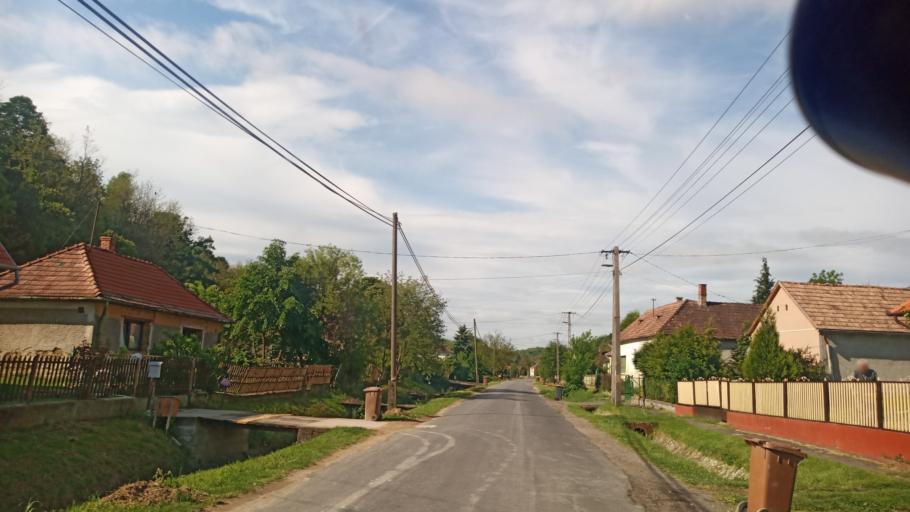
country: HU
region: Zala
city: Pacsa
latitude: 46.6719
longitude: 17.0551
